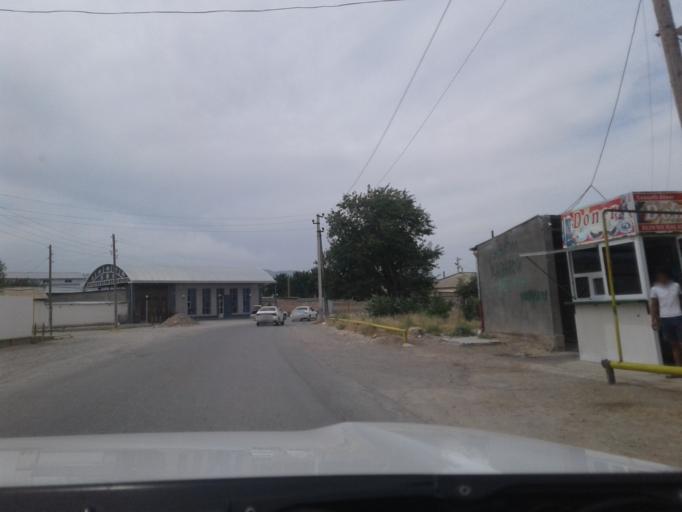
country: TM
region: Balkan
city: Serdar
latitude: 38.9848
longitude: 56.2796
